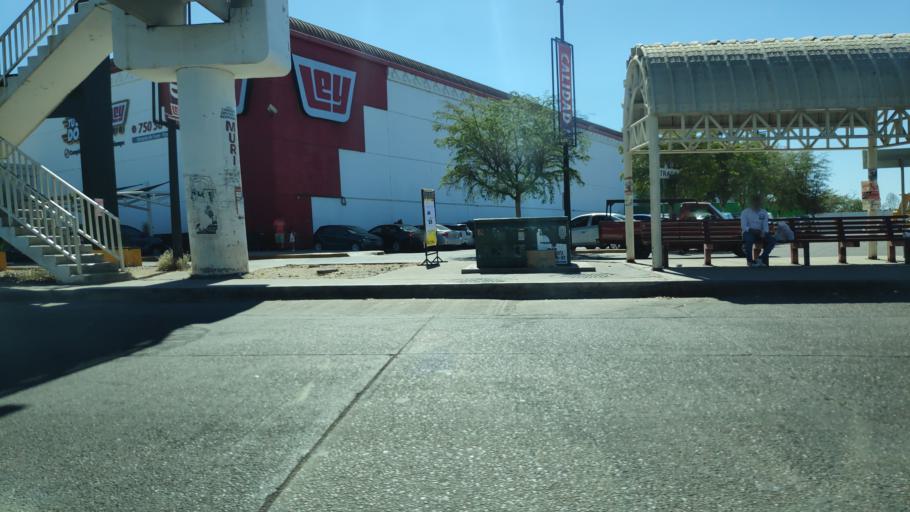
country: MX
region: Sinaloa
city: Culiacan
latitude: 24.8150
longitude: -107.4028
